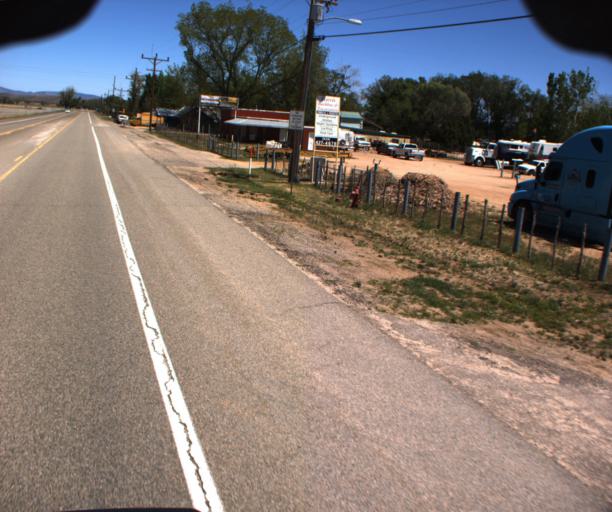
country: US
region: Arizona
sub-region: Yavapai County
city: Congress
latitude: 34.2679
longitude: -112.7272
